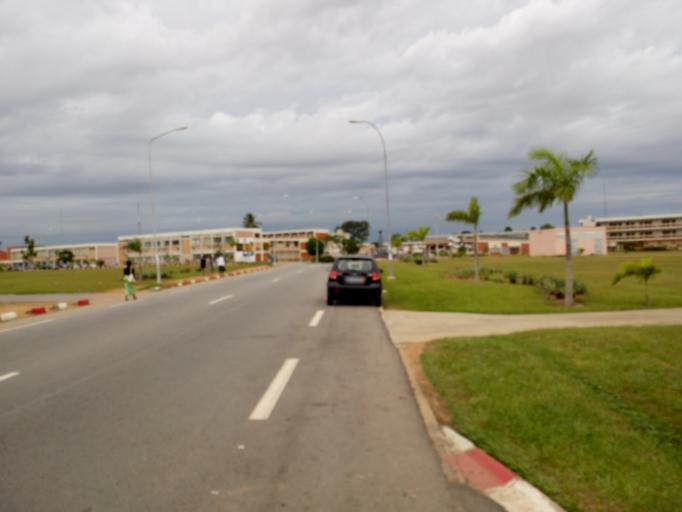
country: CI
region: Lagunes
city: Abidjan
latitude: 5.3472
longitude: -3.9876
